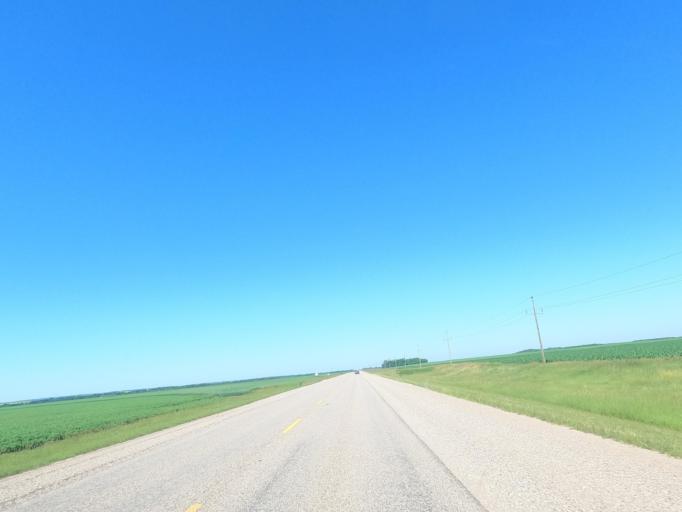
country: CA
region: Manitoba
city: Carberry
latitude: 49.5621
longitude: -99.4463
